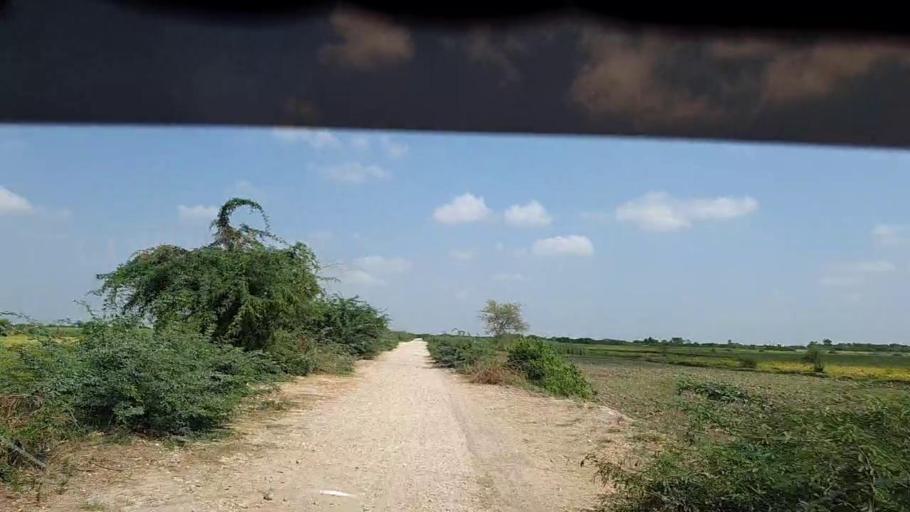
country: PK
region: Sindh
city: Kadhan
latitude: 24.6033
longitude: 68.9812
